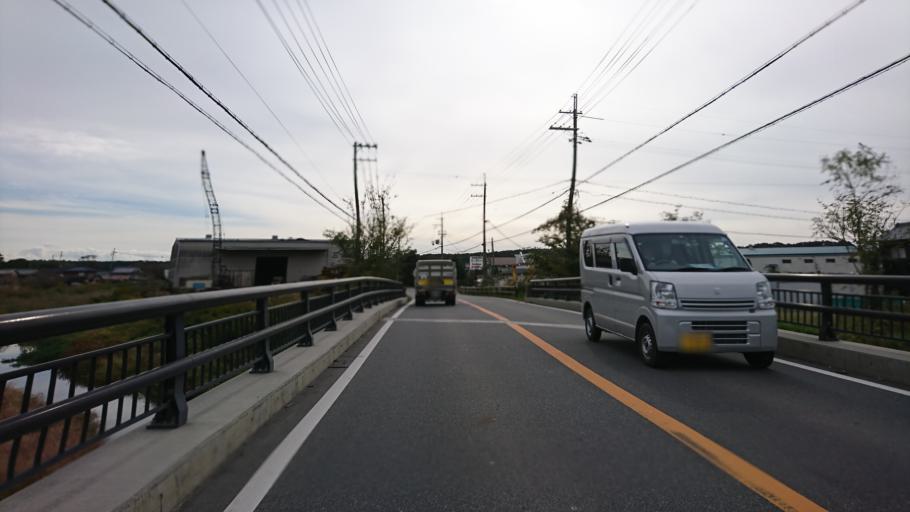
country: JP
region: Hyogo
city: Ono
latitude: 34.7871
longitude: 134.9204
